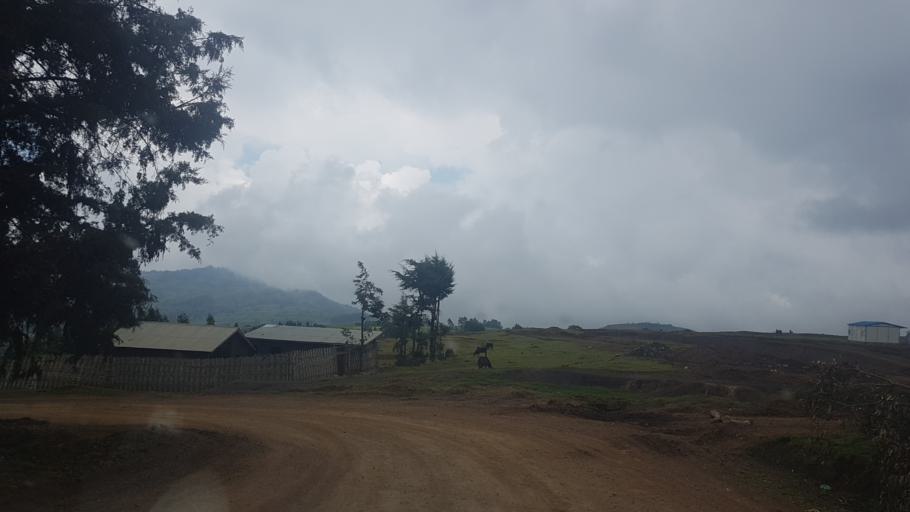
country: ET
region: Southern Nations, Nationalities, and People's Region
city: Arba Minch'
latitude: 6.3271
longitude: 37.5468
